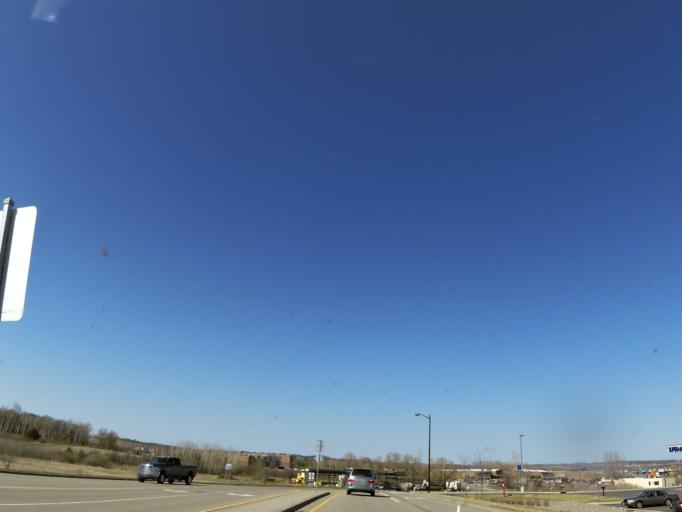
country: US
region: Minnesota
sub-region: Dakota County
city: Lakeville
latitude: 44.6455
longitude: -93.2990
